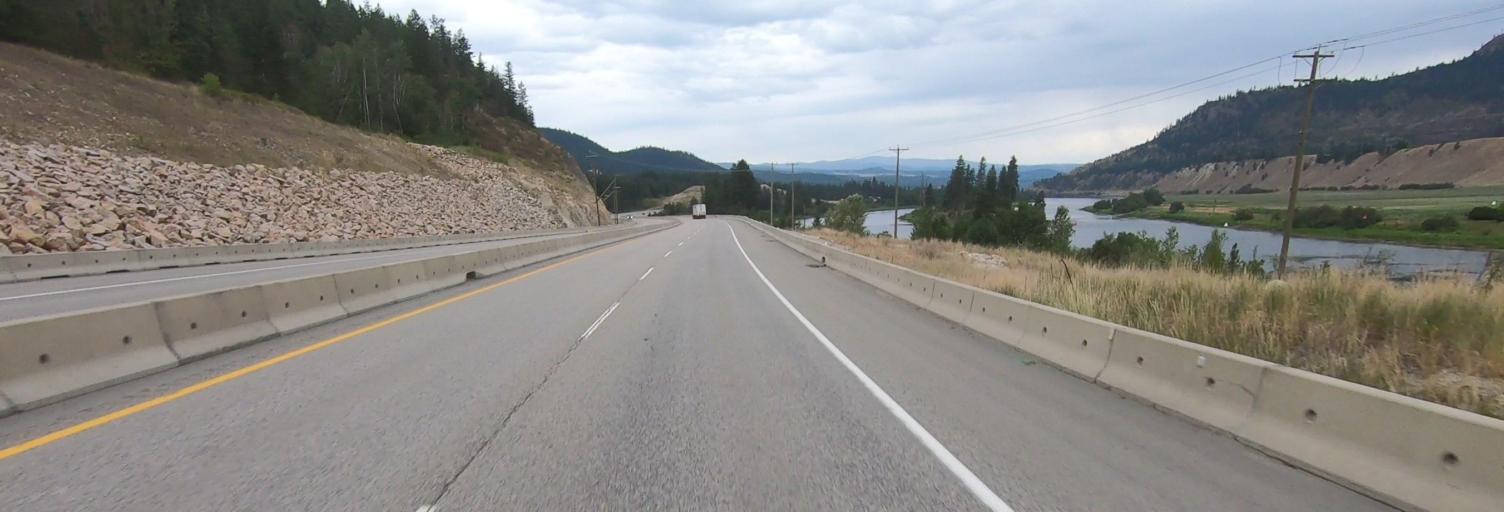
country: CA
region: British Columbia
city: Chase
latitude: 50.7323
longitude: -119.7641
